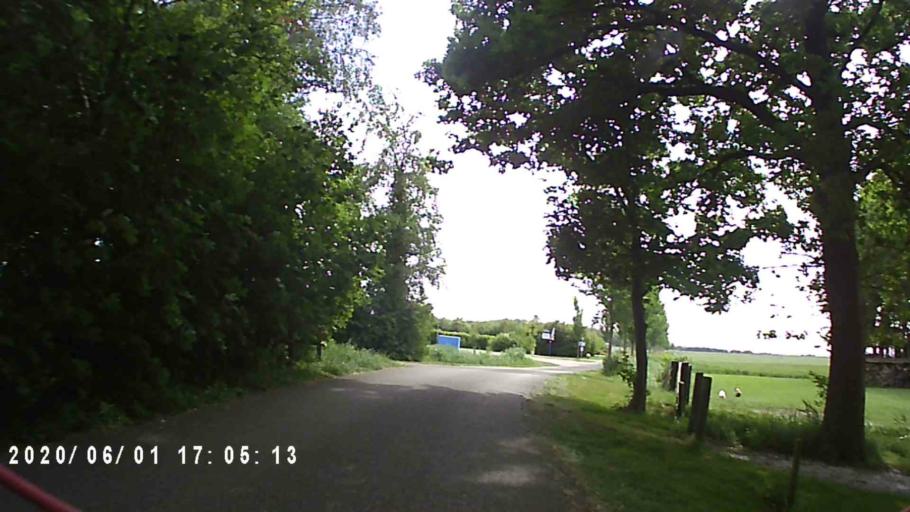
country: NL
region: Friesland
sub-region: Gemeente Tytsjerksteradiel
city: Garyp
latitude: 53.1722
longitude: 5.9340
